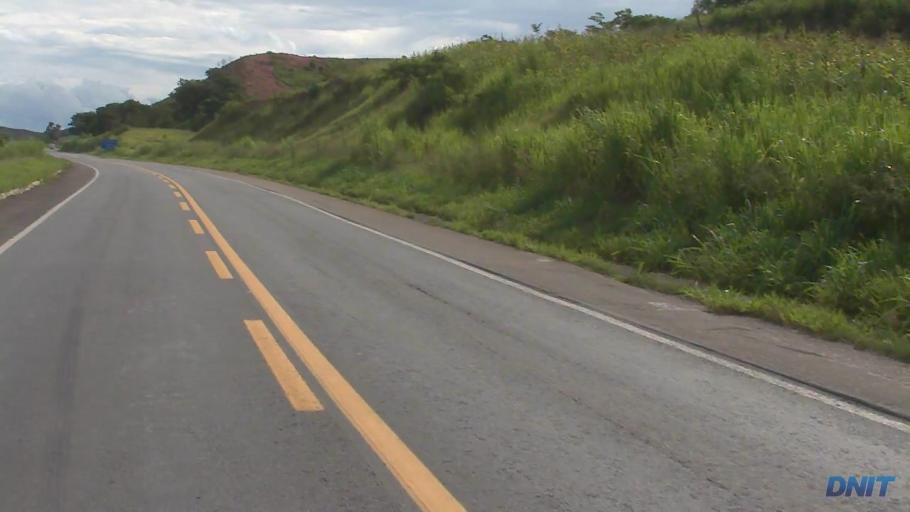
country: BR
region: Minas Gerais
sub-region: Belo Oriente
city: Belo Oriente
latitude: -19.1904
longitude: -42.2727
